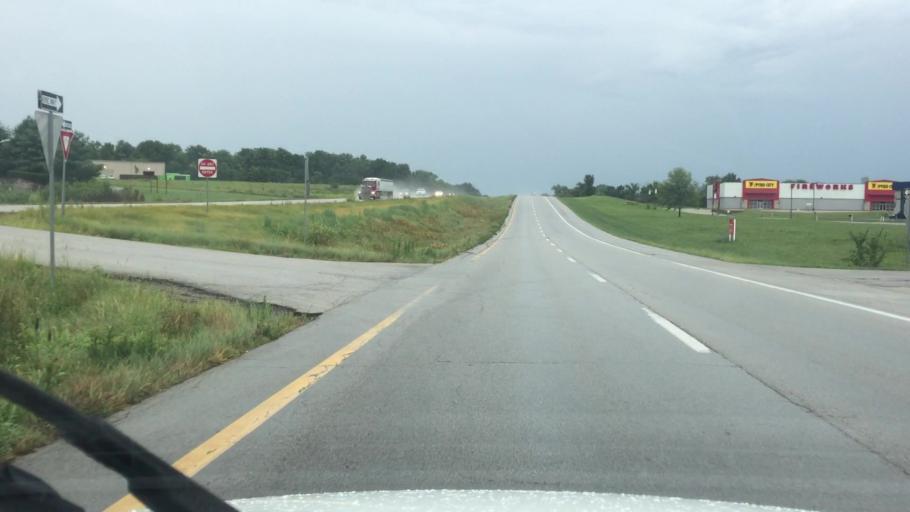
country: US
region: Missouri
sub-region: Jackson County
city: Lone Jack
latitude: 38.8799
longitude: -94.2147
